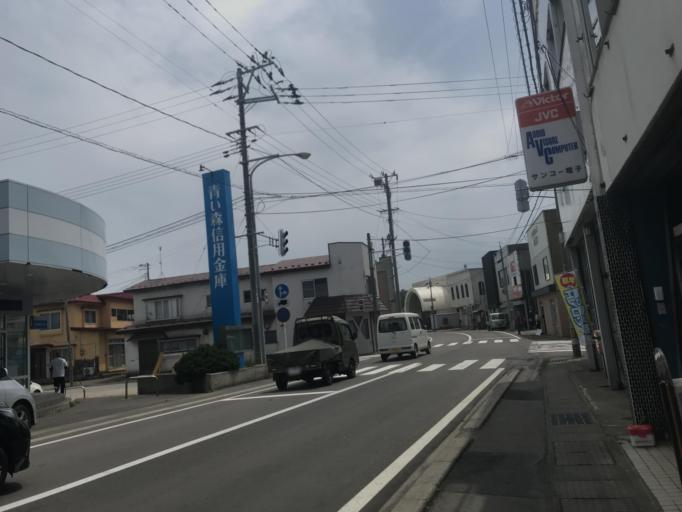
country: JP
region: Aomori
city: Shimokizukuri
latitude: 40.7772
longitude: 140.2193
